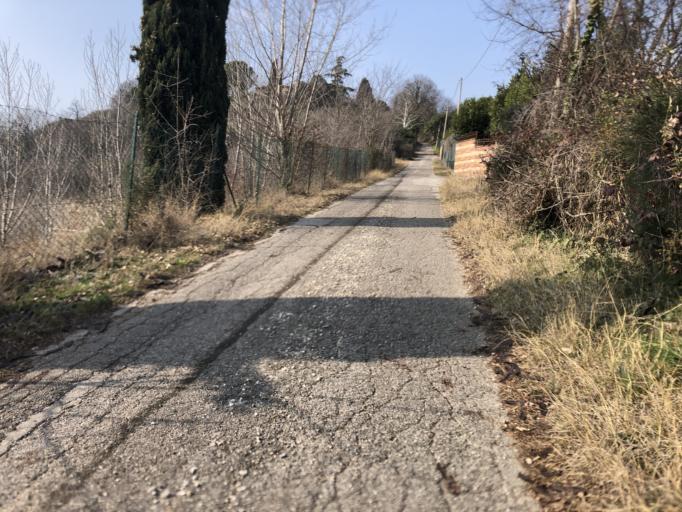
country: IT
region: Veneto
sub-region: Provincia di Verona
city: Sona
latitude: 45.4268
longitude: 10.8413
